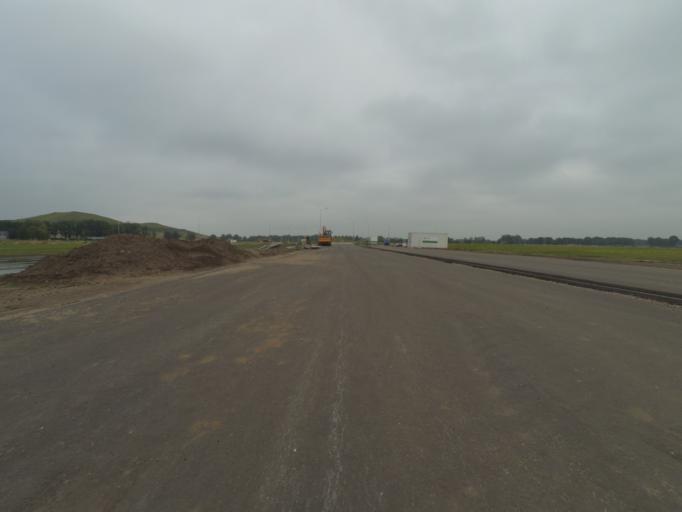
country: NL
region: Gelderland
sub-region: Gemeente Barneveld
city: Voorthuizen
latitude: 52.1613
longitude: 5.6182
